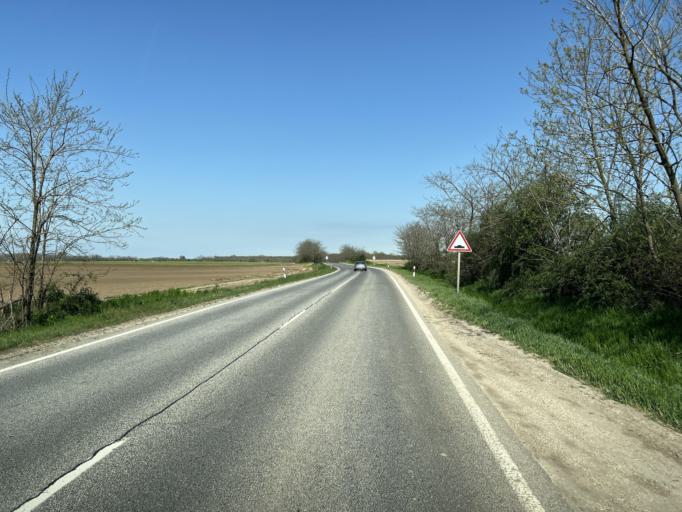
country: HU
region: Pest
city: Alsonemedi
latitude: 47.3221
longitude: 19.1954
